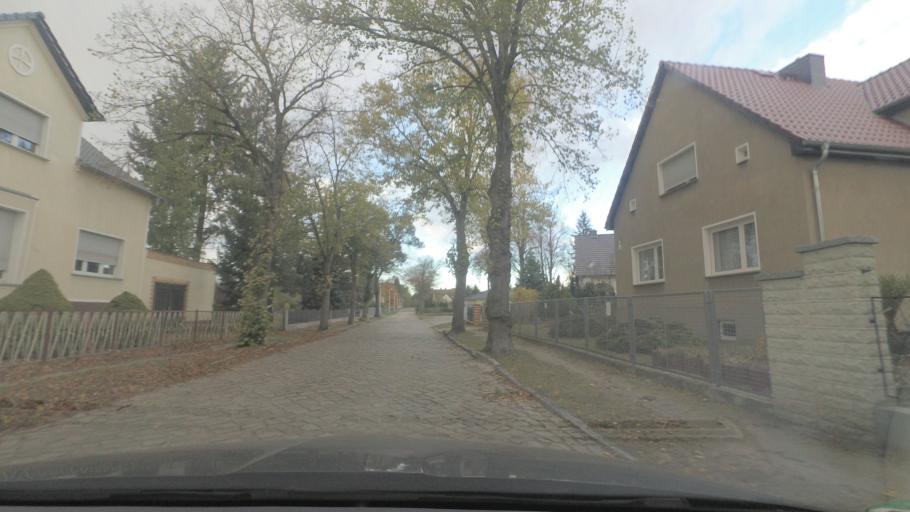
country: DE
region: Brandenburg
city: Zossen
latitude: 52.1622
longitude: 13.4623
